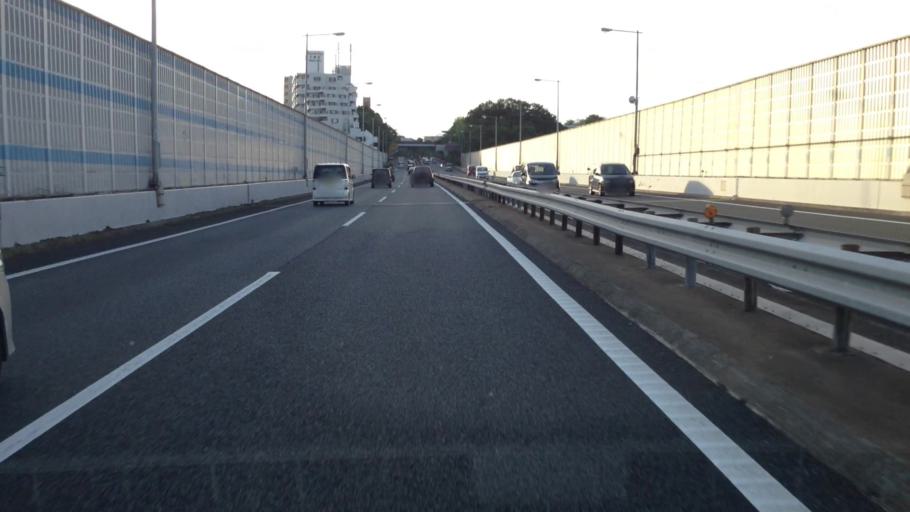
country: JP
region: Kanagawa
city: Kamakura
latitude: 35.3852
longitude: 139.5810
